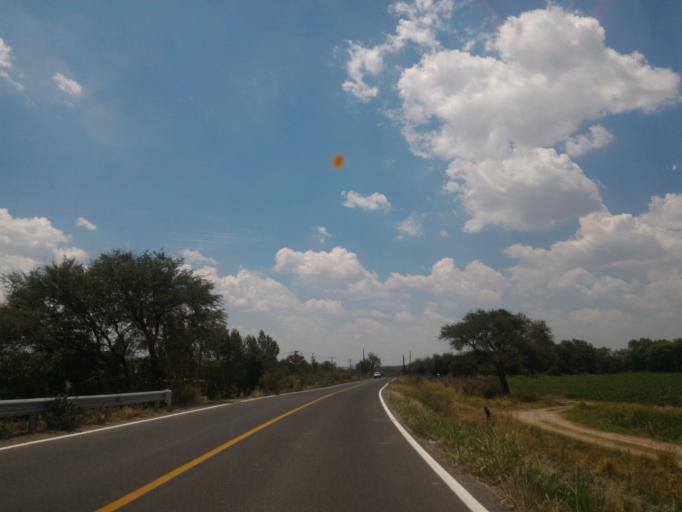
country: MX
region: Guanajuato
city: Ciudad Manuel Doblado
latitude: 20.7878
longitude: -101.9824
